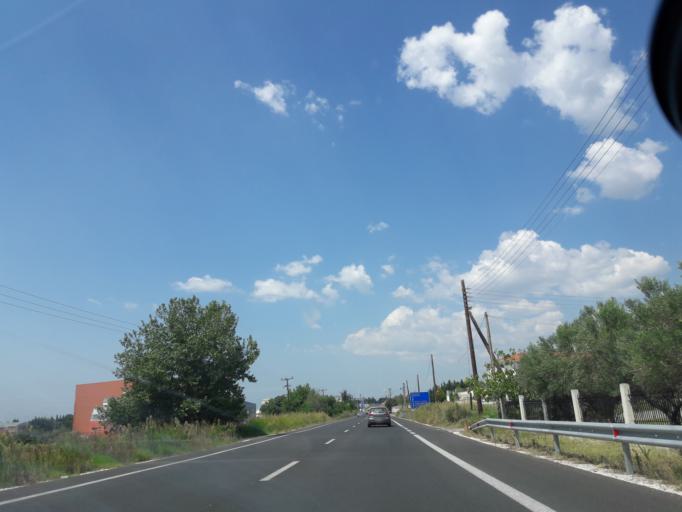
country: GR
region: Central Macedonia
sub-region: Nomos Thessalonikis
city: Agia Paraskevi
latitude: 40.5156
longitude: 23.0704
